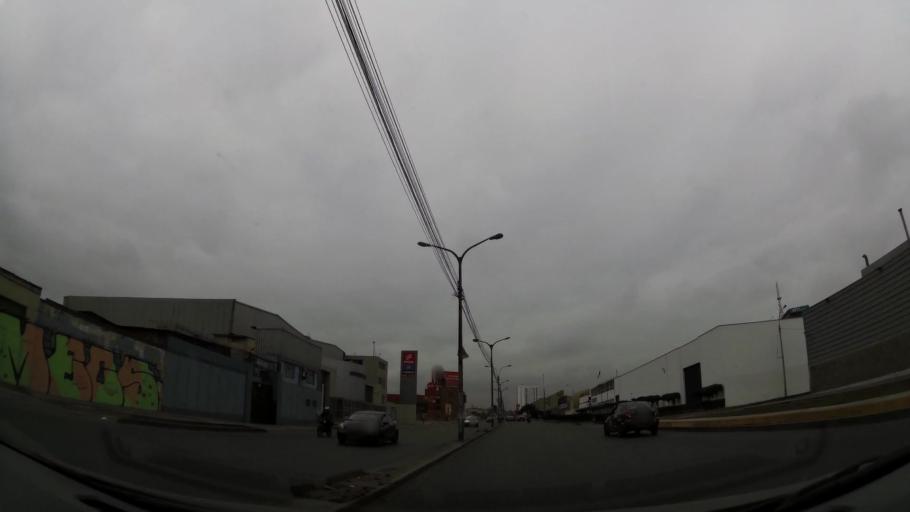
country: PE
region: Lima
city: Lima
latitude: -12.0479
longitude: -77.0584
